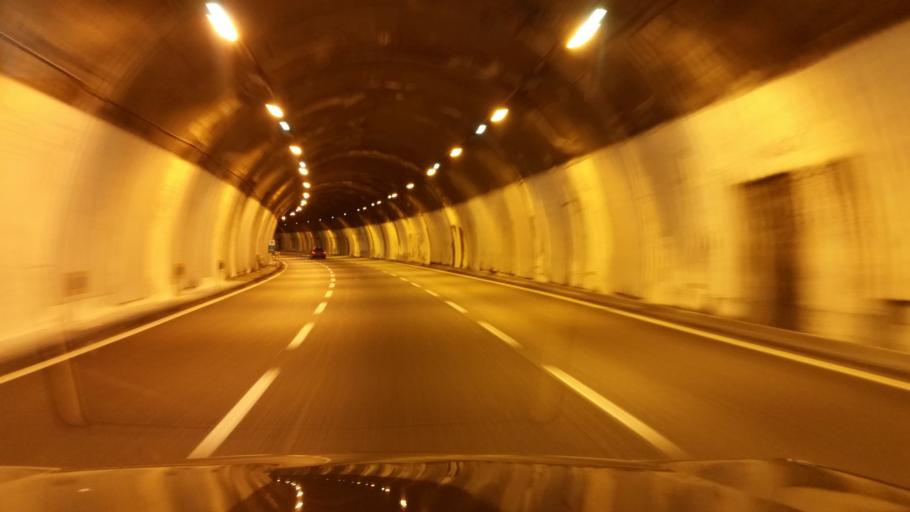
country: IT
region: Liguria
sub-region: Provincia di Genova
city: Mele
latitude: 44.4432
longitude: 8.7180
